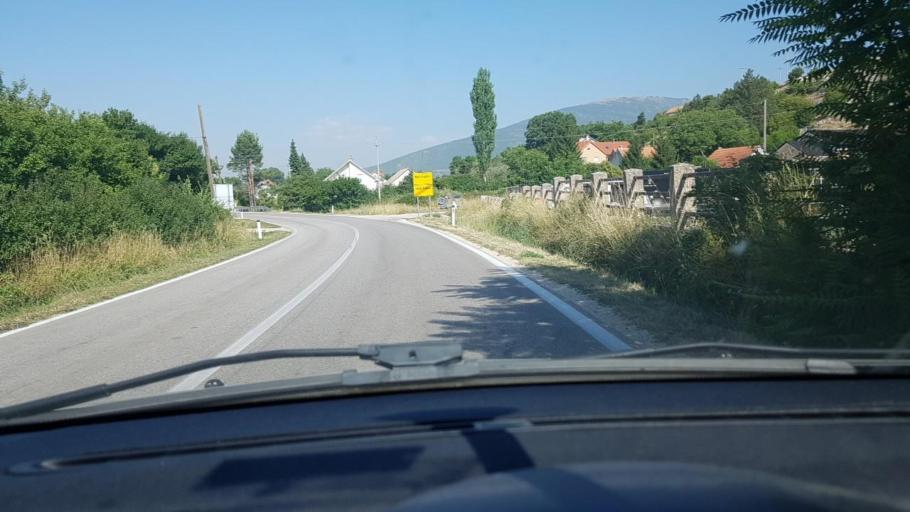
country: BA
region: Federation of Bosnia and Herzegovina
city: Zabrisce
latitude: 43.8536
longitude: 16.9492
